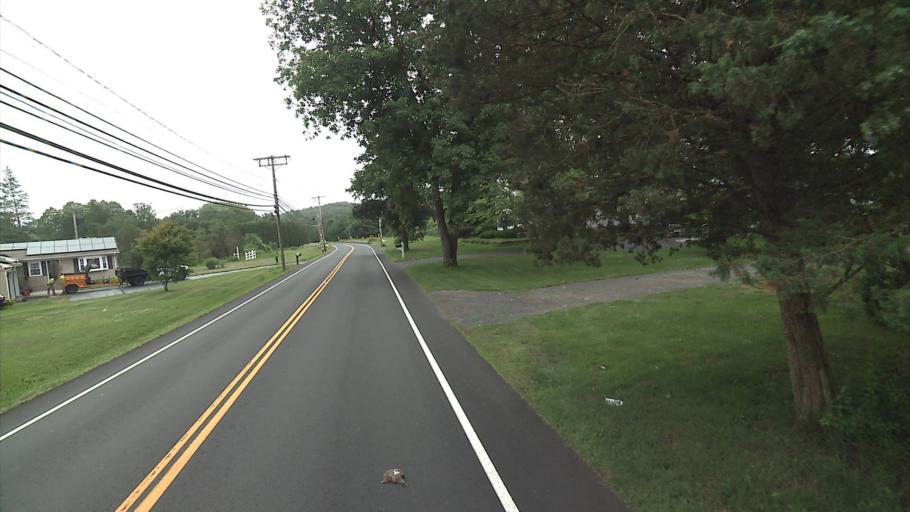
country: US
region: Connecticut
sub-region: Hartford County
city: Glastonbury Center
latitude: 41.7160
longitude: -72.5539
